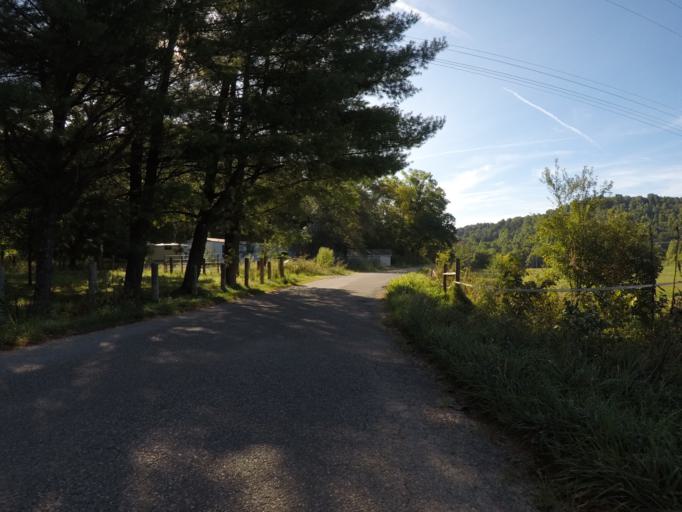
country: US
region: Ohio
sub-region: Lawrence County
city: Burlington
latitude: 38.5015
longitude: -82.5131
